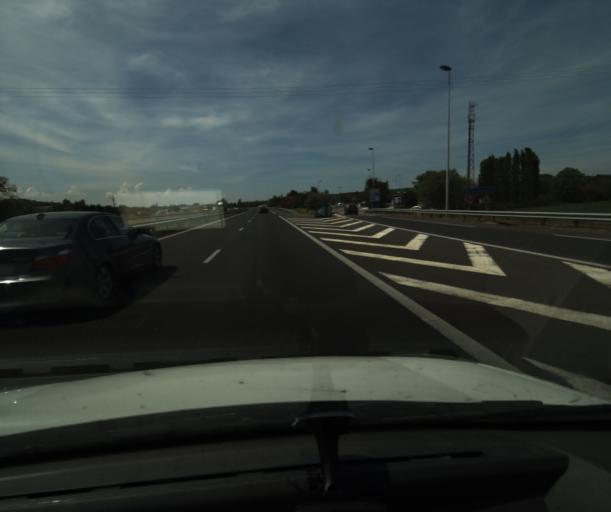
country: FR
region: Midi-Pyrenees
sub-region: Departement de la Haute-Garonne
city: Avignonet-Lauragais
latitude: 43.3512
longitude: 1.8112
